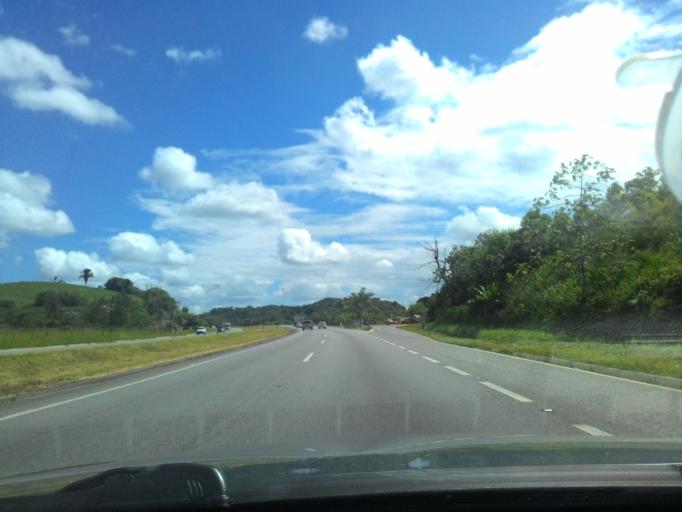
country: BR
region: Sao Paulo
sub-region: Registro
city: Registro
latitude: -24.5748
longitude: -47.8833
